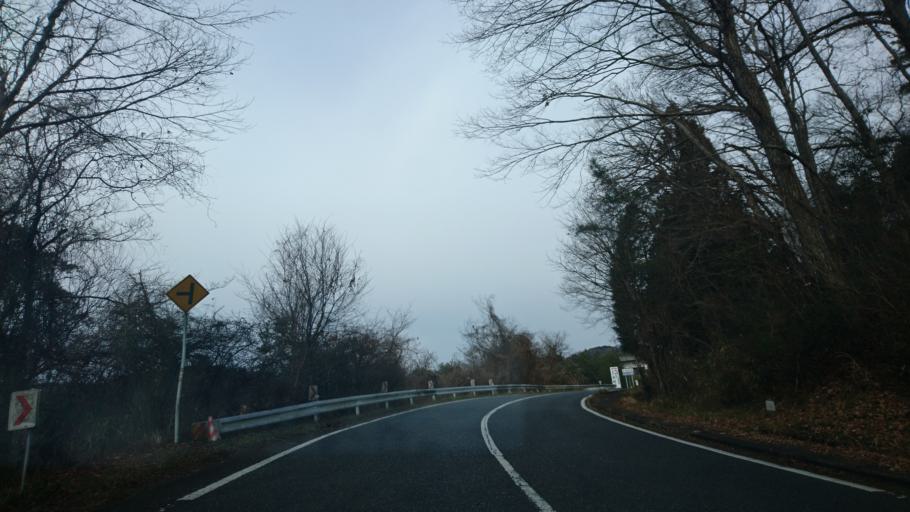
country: JP
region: Okayama
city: Takahashi
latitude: 34.8261
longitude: 133.6656
